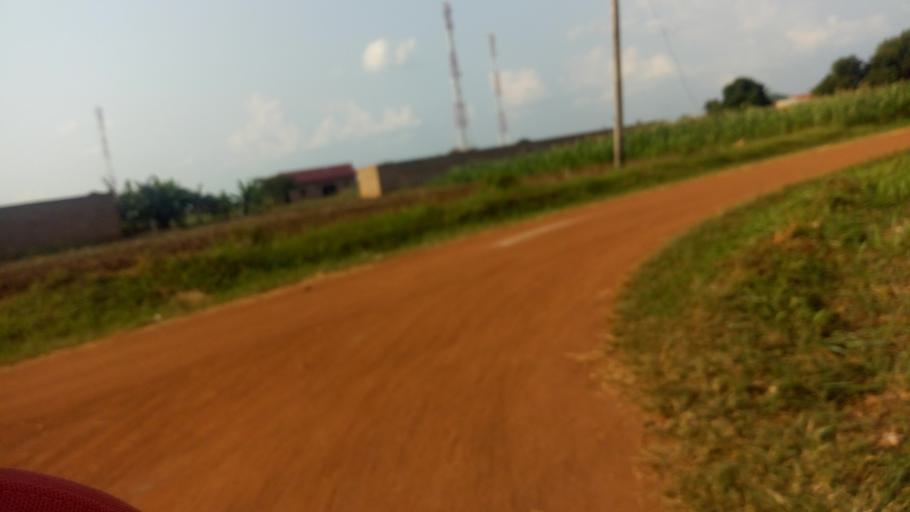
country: UG
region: Western Region
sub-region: Kiryandongo District
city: Kiryandongo
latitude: 1.8054
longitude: 32.0081
